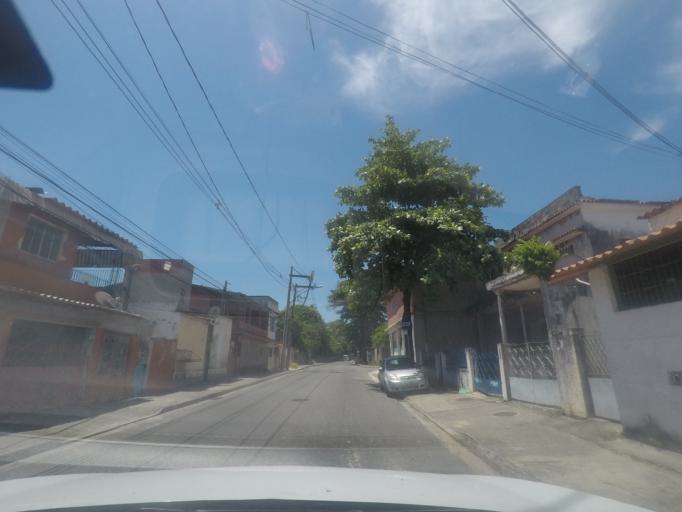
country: BR
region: Rio de Janeiro
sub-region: Itaguai
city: Itaguai
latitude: -22.9830
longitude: -43.6853
